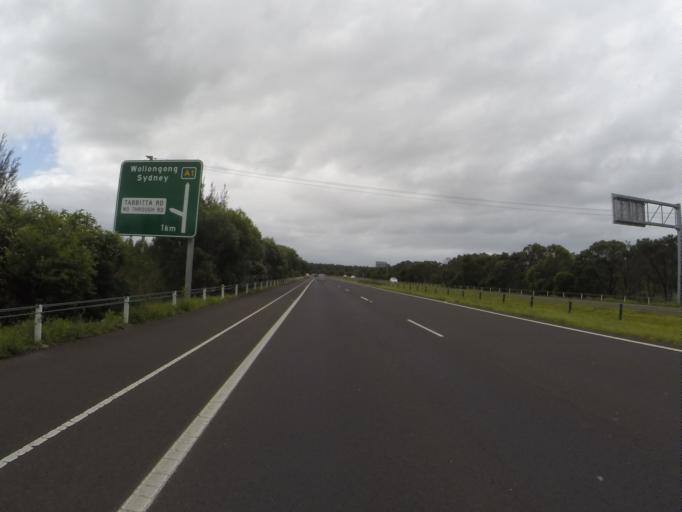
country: AU
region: New South Wales
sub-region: Shellharbour
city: Croom
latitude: -34.6212
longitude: 150.8375
